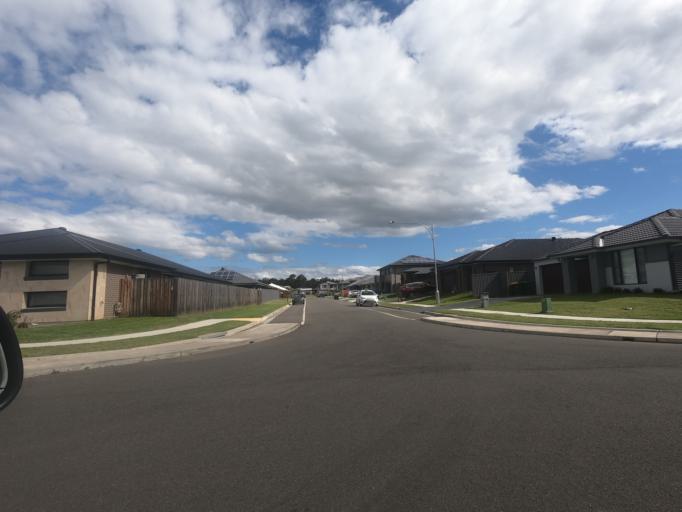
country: AU
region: New South Wales
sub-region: Wollongong
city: Dapto
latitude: -34.4859
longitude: 150.7656
